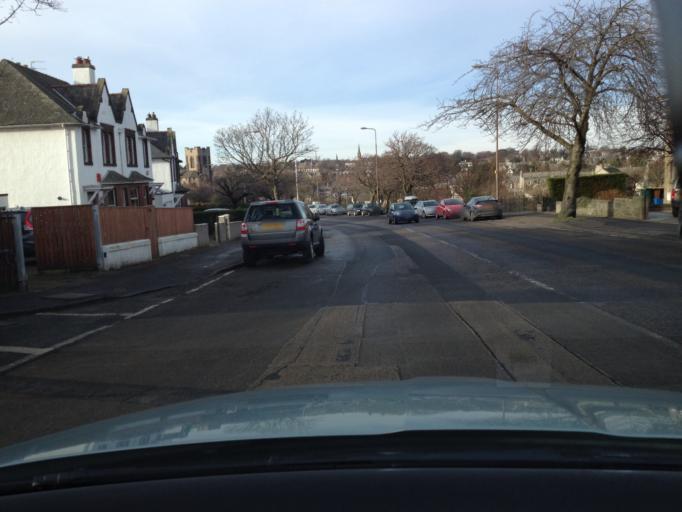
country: GB
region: Scotland
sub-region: Edinburgh
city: Edinburgh
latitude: 55.9251
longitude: -3.1813
